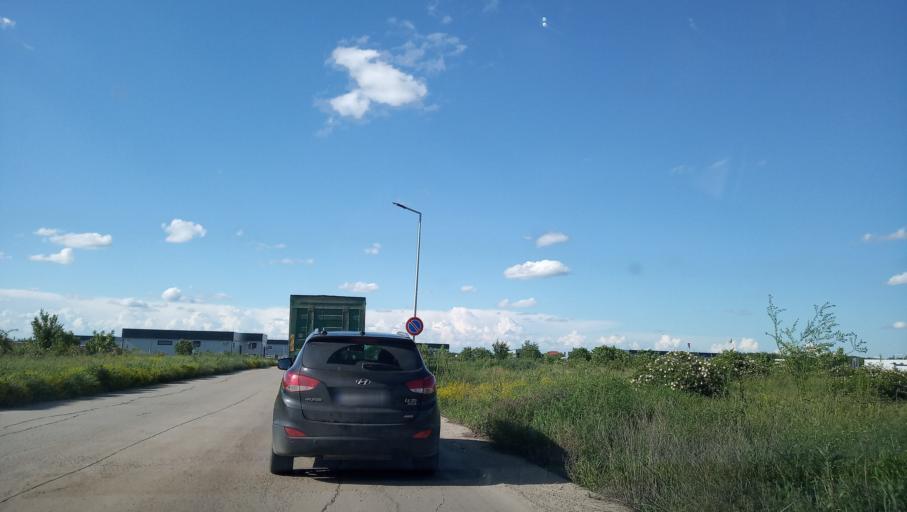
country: RO
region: Ilfov
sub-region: Comuna Dragomiresti-Vale
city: Dragomiresti-Deal
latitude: 44.4491
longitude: 25.9579
